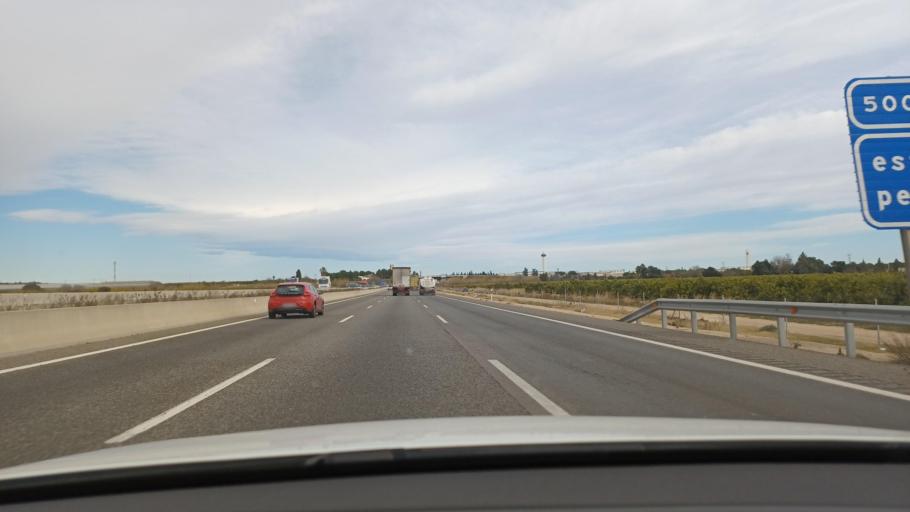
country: ES
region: Valencia
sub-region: Provincia de Valencia
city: Benifaio
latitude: 39.3057
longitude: -0.4453
